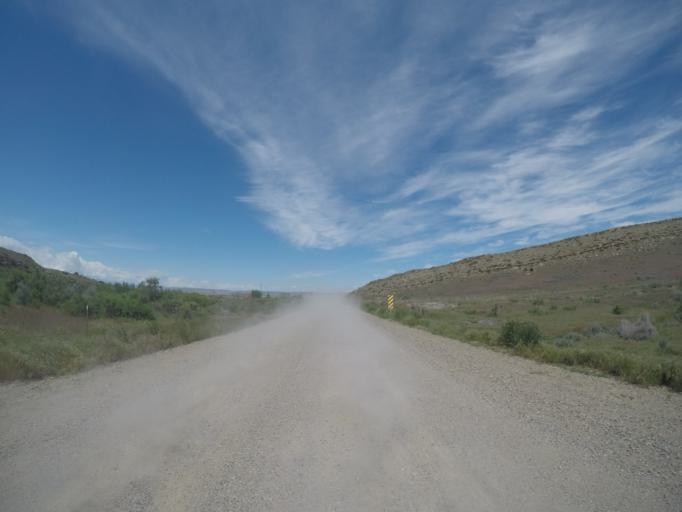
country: US
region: Montana
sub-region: Carbon County
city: Red Lodge
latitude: 45.2416
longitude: -108.8595
